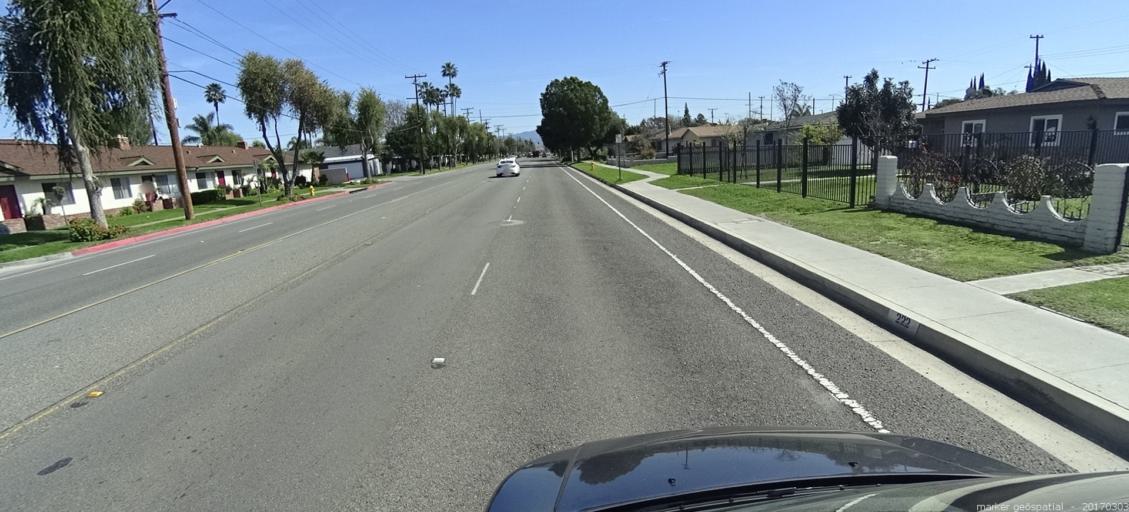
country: US
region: California
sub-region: Orange County
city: Garden Grove
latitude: 33.7961
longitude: -117.9094
